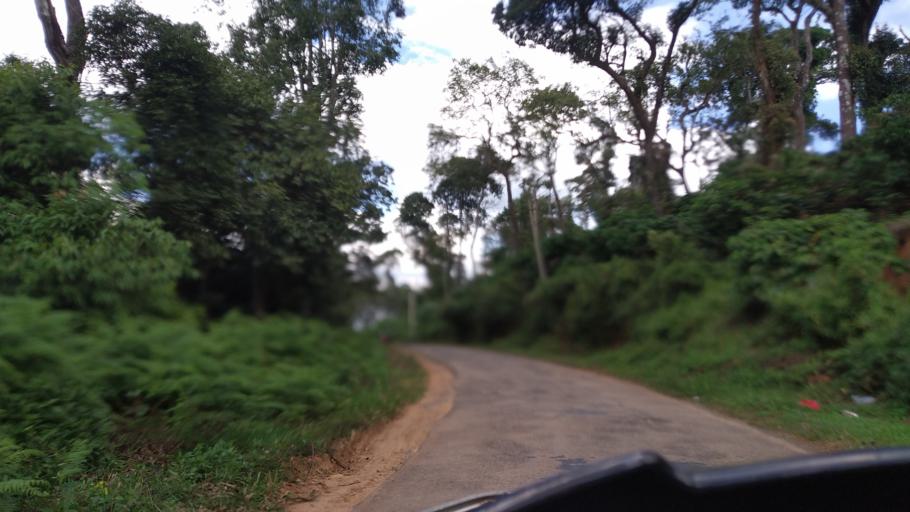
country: IN
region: Karnataka
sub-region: Kodagu
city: Ponnampet
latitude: 12.0357
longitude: 75.9050
